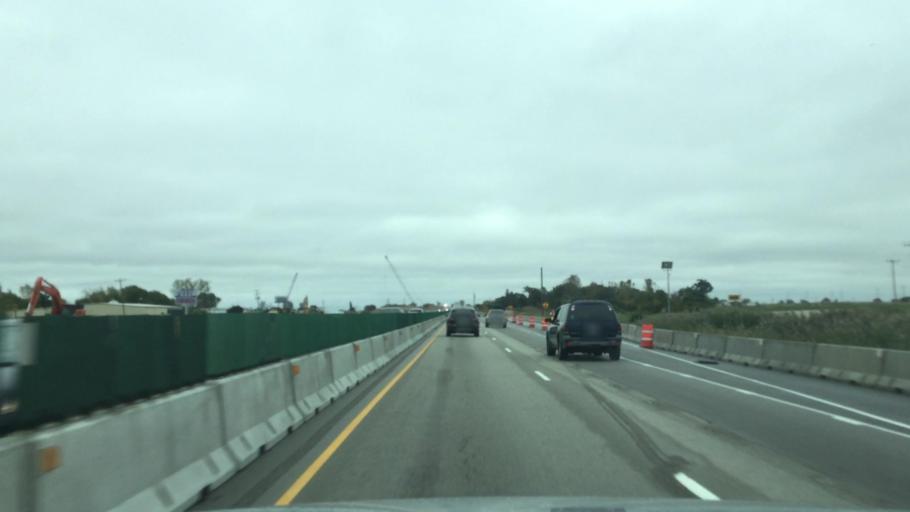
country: US
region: Wisconsin
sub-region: Kenosha County
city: Somers
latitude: 42.6465
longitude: -87.9528
